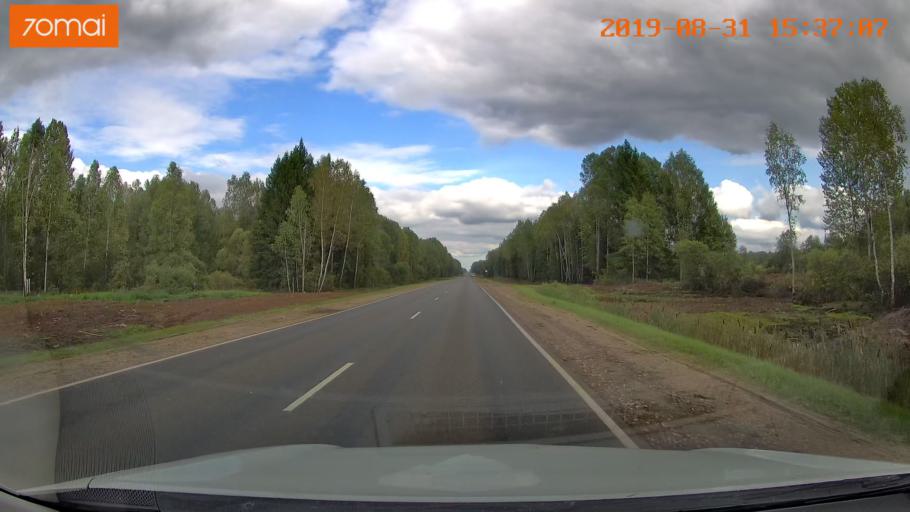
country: RU
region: Kaluga
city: Mosal'sk
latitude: 54.6160
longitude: 34.7761
